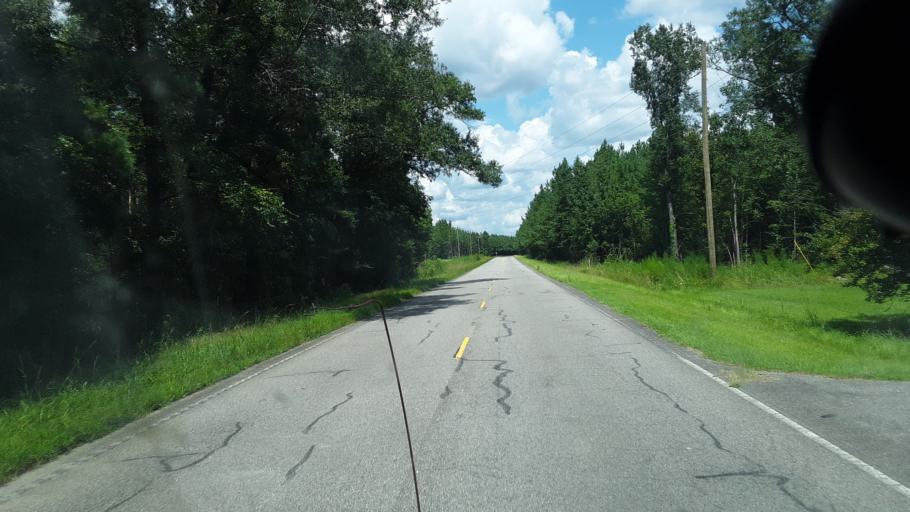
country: US
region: South Carolina
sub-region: Williamsburg County
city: Andrews
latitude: 33.5317
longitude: -79.4866
